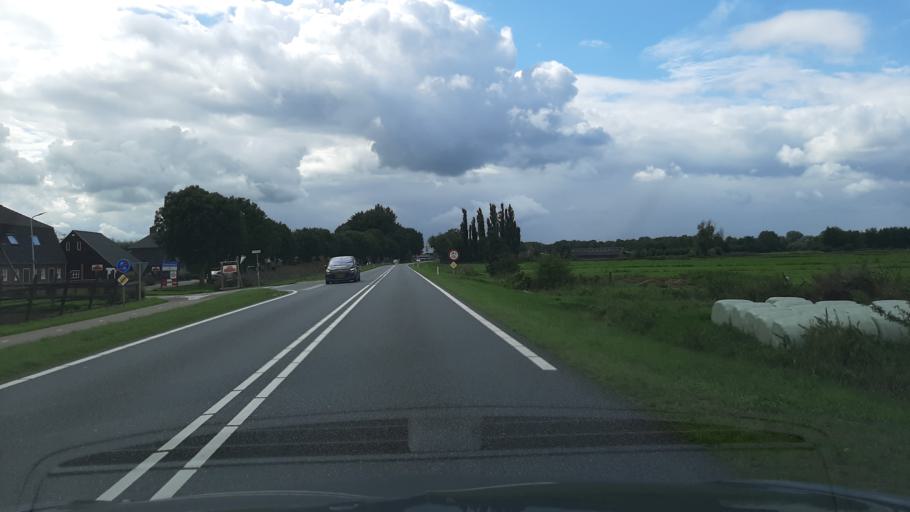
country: NL
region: Overijssel
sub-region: Gemeente Zwartewaterland
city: Hasselt
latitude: 52.6498
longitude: 6.0884
